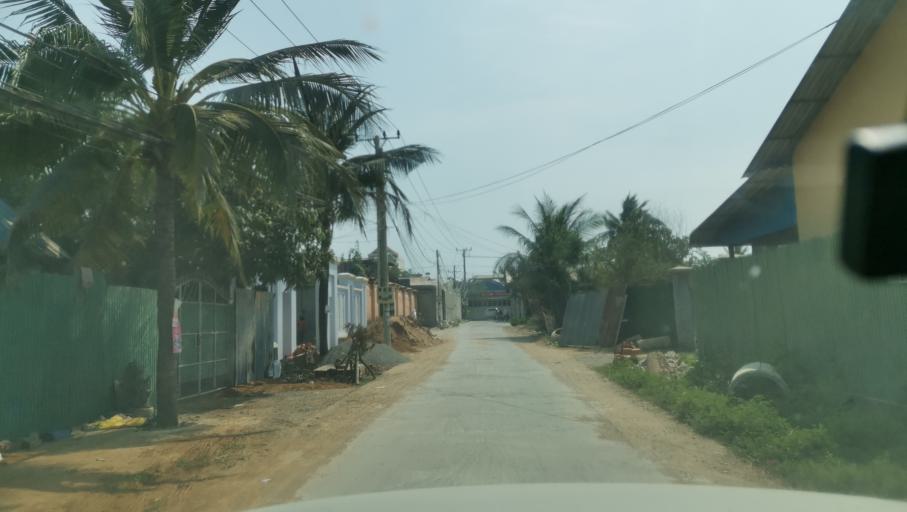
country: KH
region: Battambang
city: Battambang
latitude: 13.0854
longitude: 103.1930
